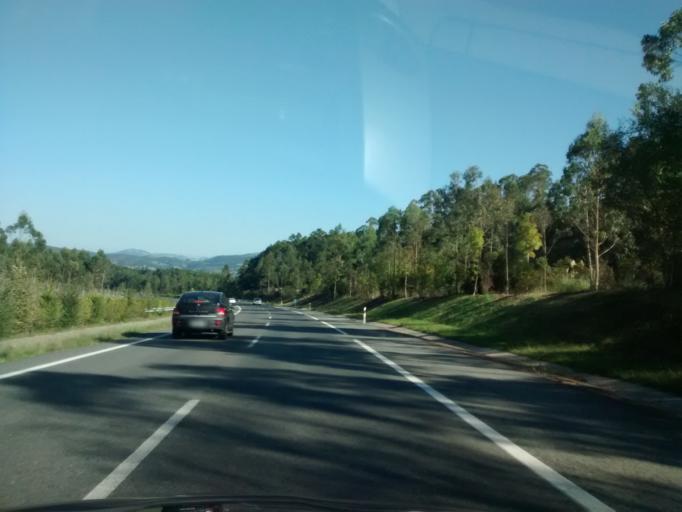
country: ES
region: Cantabria
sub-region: Provincia de Cantabria
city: Cabezon de la Sal
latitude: 43.3212
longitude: -4.2159
